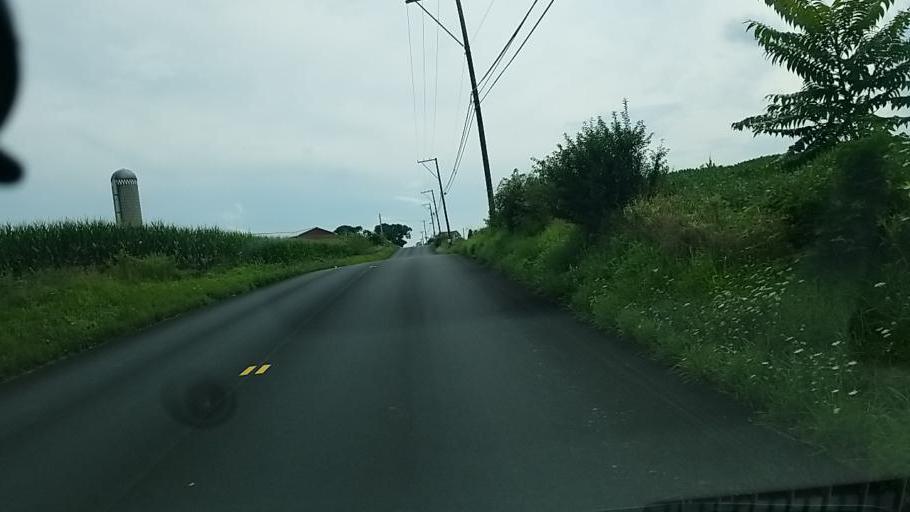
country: US
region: Pennsylvania
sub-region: Dauphin County
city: Elizabethville
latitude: 40.5903
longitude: -76.8113
